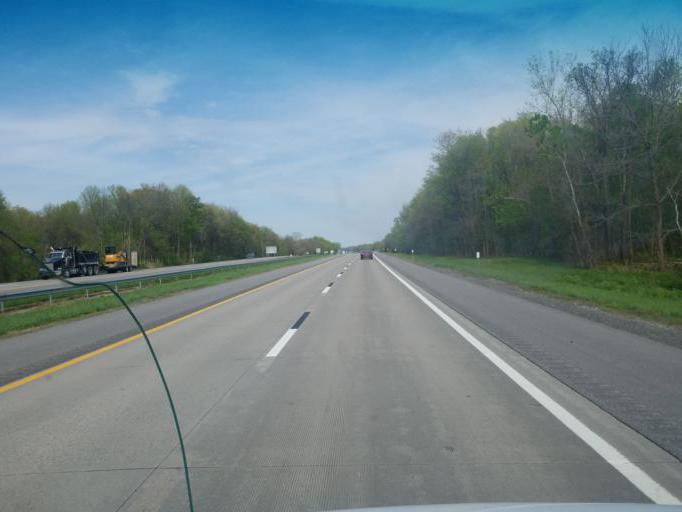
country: US
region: New York
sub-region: Cayuga County
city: Weedsport
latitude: 43.0641
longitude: -76.5492
